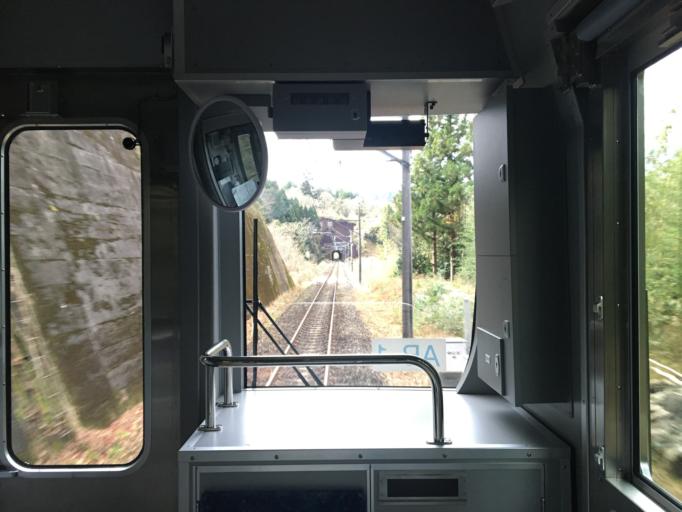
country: JP
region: Miyagi
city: Marumori
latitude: 37.9286
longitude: 140.6970
